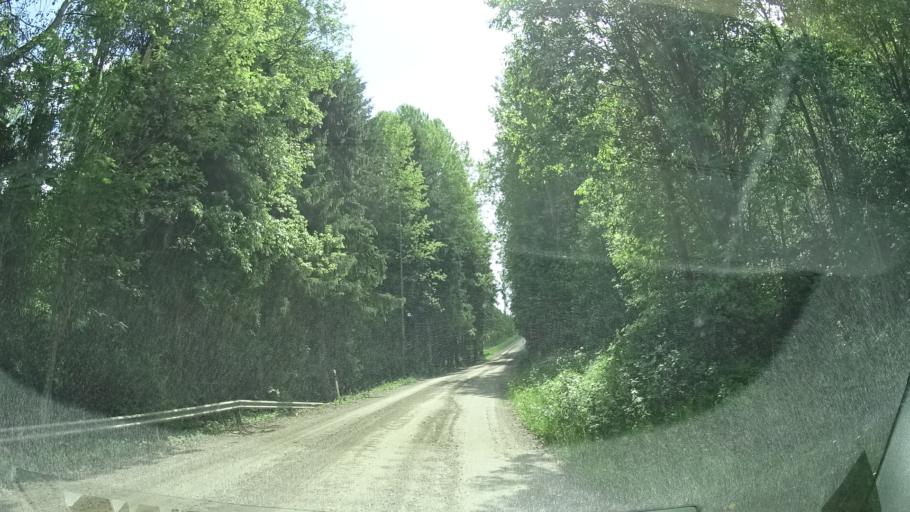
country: FI
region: Uusimaa
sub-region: Helsinki
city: Siuntio
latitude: 60.2128
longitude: 24.2885
